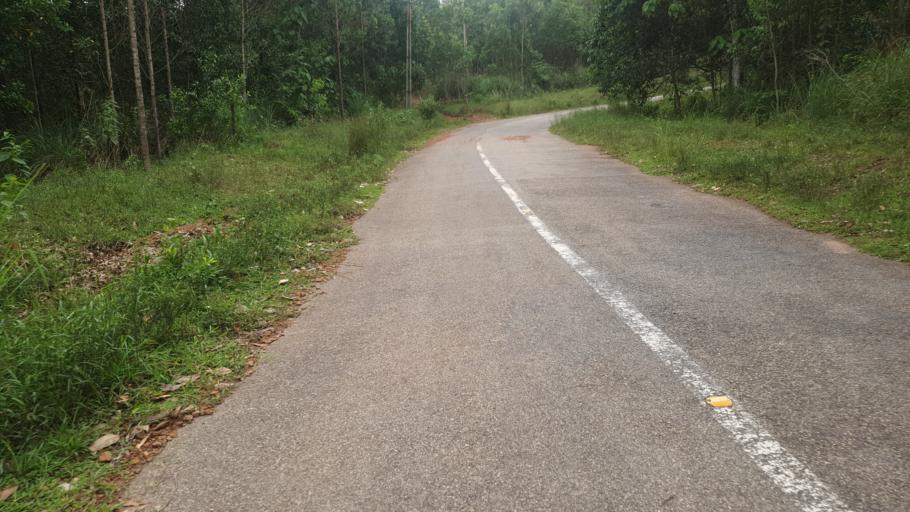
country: IN
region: Kerala
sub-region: Thiruvananthapuram
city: Nedumangad
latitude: 8.6359
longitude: 77.1113
